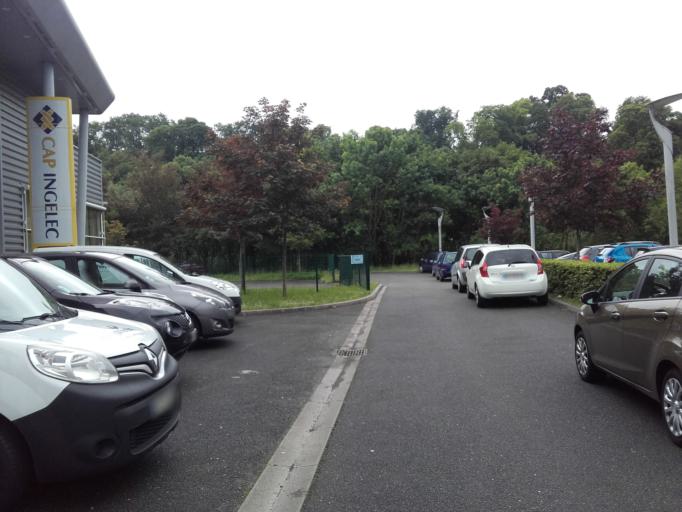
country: FR
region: Centre
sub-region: Departement d'Indre-et-Loire
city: Joue-les-Tours
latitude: 47.3633
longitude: 0.6808
